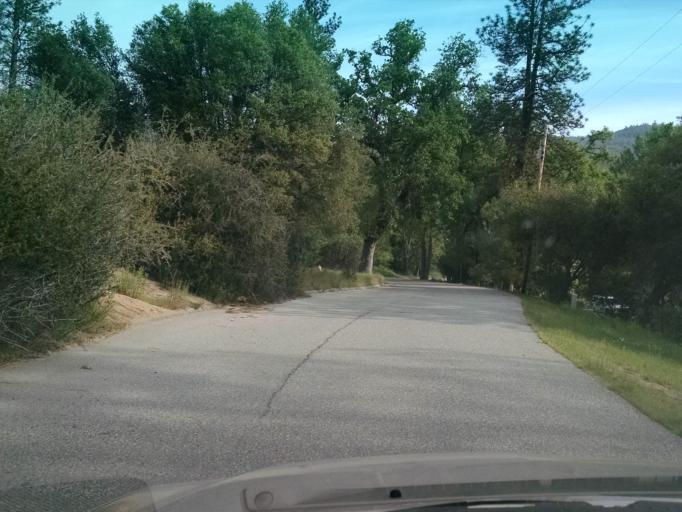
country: US
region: California
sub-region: Madera County
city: Oakhurst
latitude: 37.3232
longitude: -119.6288
